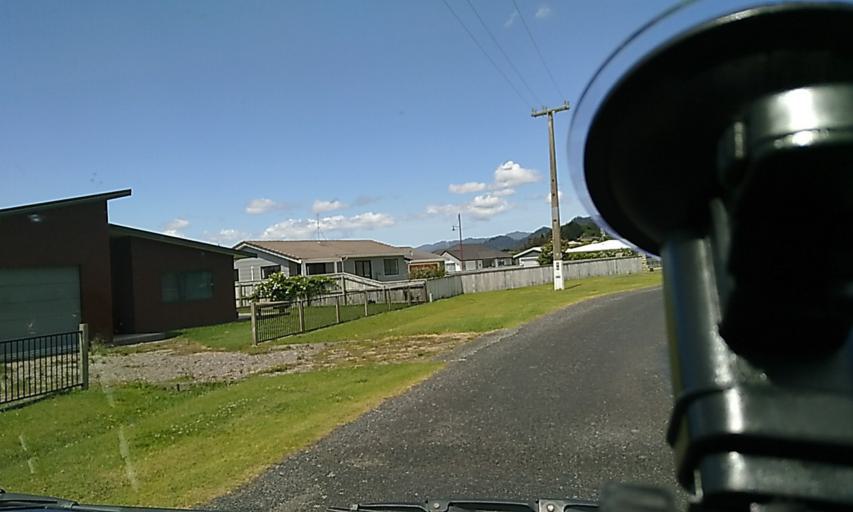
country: NZ
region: Bay of Plenty
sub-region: Western Bay of Plenty District
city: Waihi Beach
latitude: -37.4463
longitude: 175.9604
